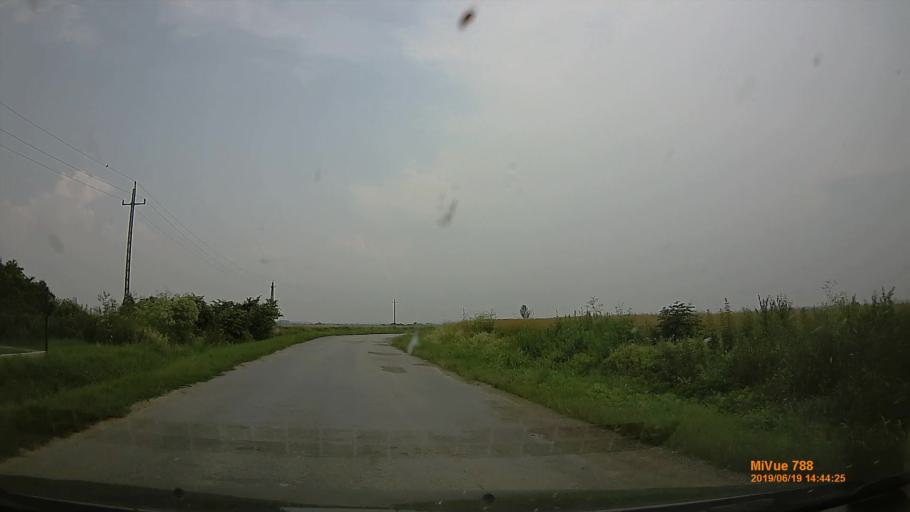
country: HU
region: Baranya
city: Szigetvar
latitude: 46.0282
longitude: 17.8279
